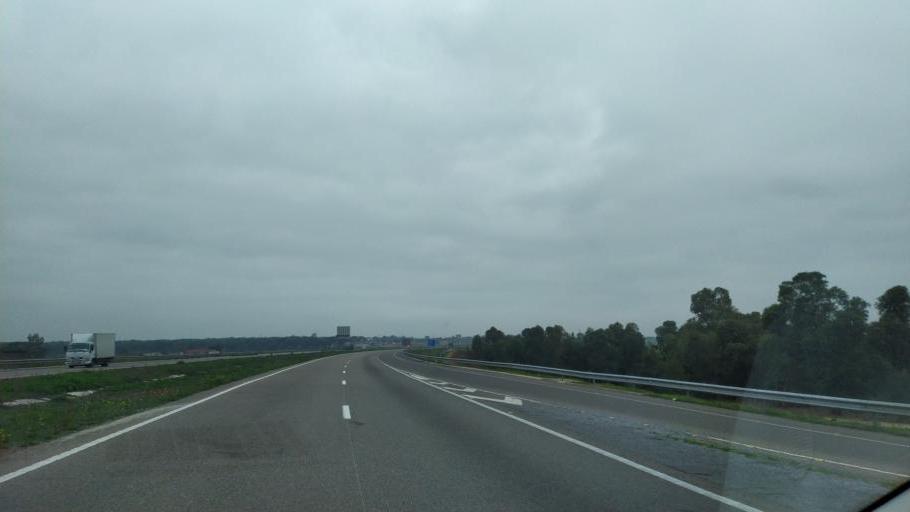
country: MA
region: Rabat-Sale-Zemmour-Zaer
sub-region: Skhirate-Temara
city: Temara
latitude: 33.8463
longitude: -6.8982
